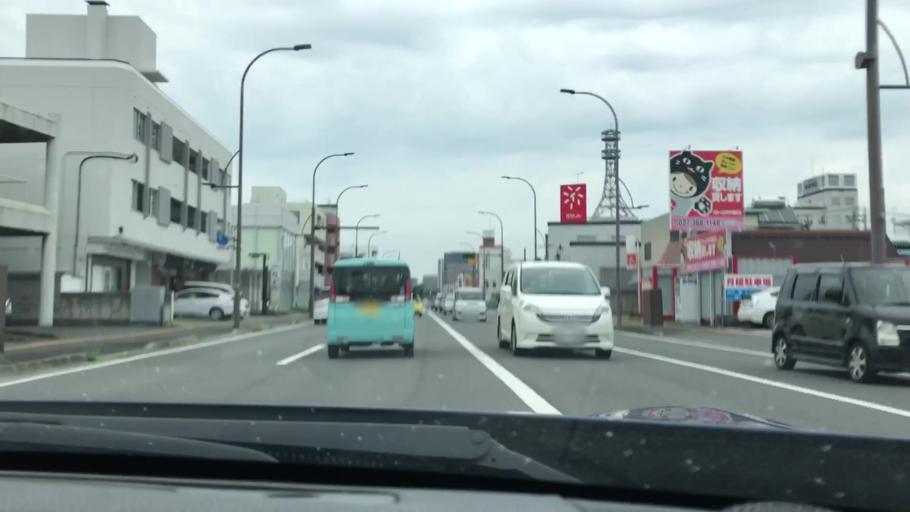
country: JP
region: Gunma
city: Maebashi-shi
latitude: 36.3782
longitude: 139.0697
